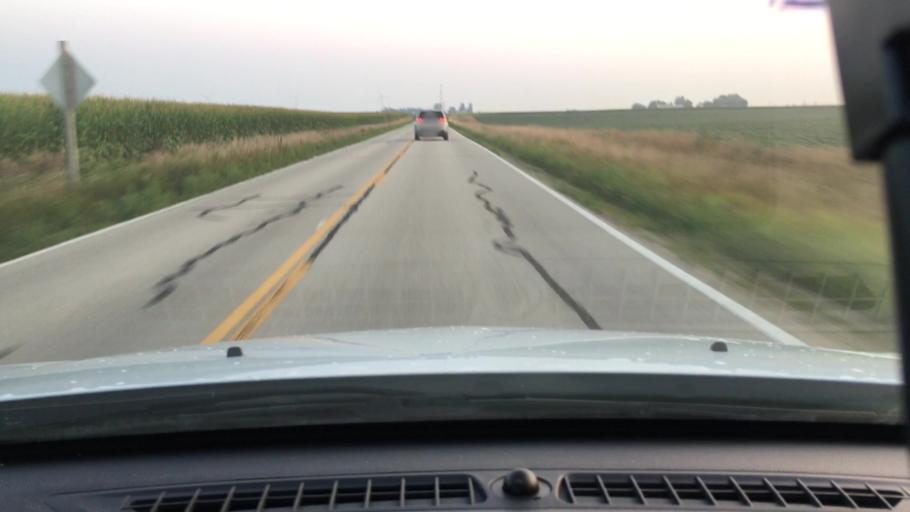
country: US
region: Illinois
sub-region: DeKalb County
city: Malta
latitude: 41.8514
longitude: -88.8478
